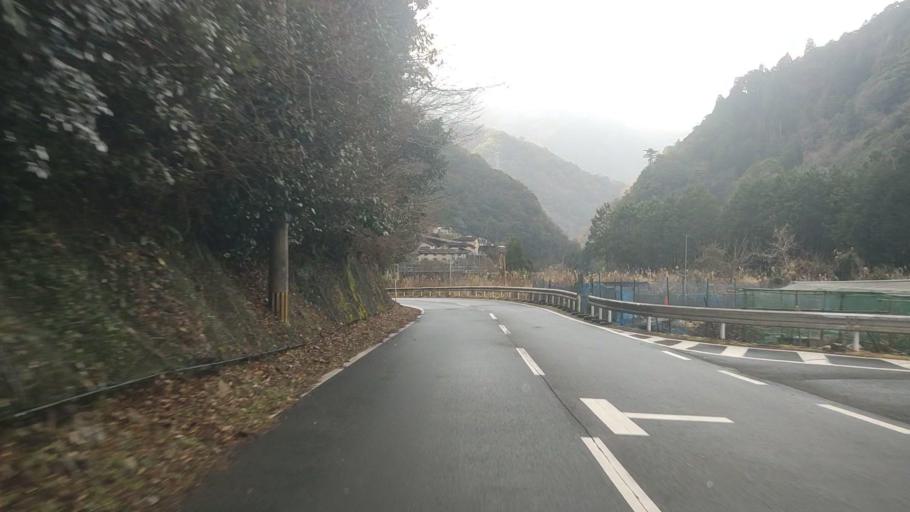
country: JP
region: Kumamoto
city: Hitoyoshi
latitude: 32.4297
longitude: 130.8585
